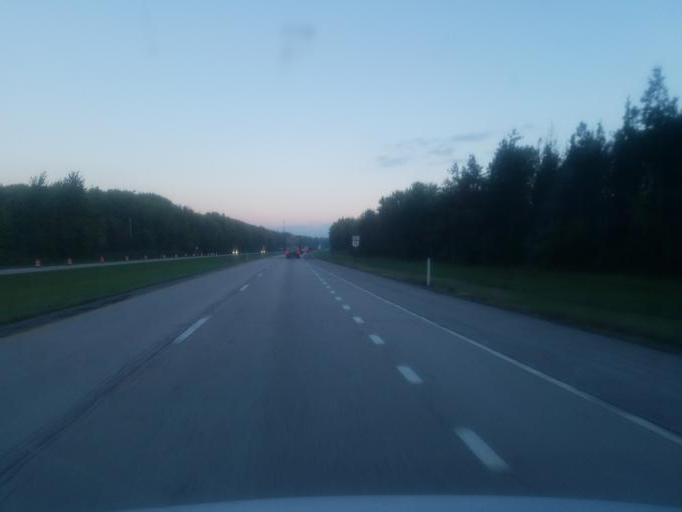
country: US
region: Ohio
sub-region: Ashtabula County
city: Ashtabula
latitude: 41.8133
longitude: -80.7613
